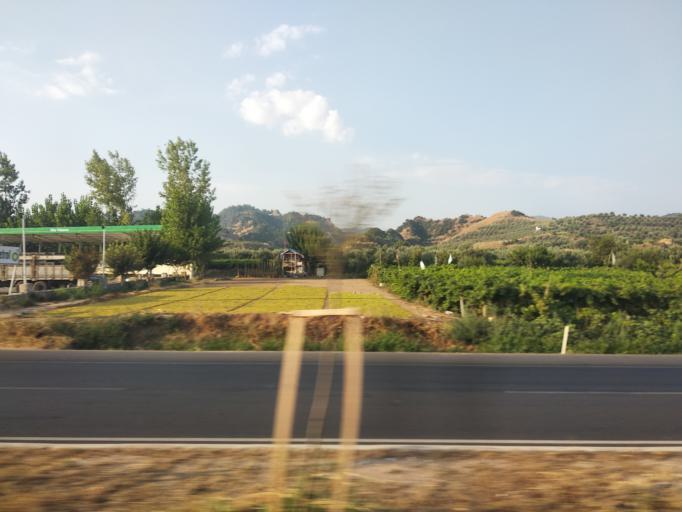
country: TR
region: Manisa
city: Ahmetli
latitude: 38.5075
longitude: 27.9906
